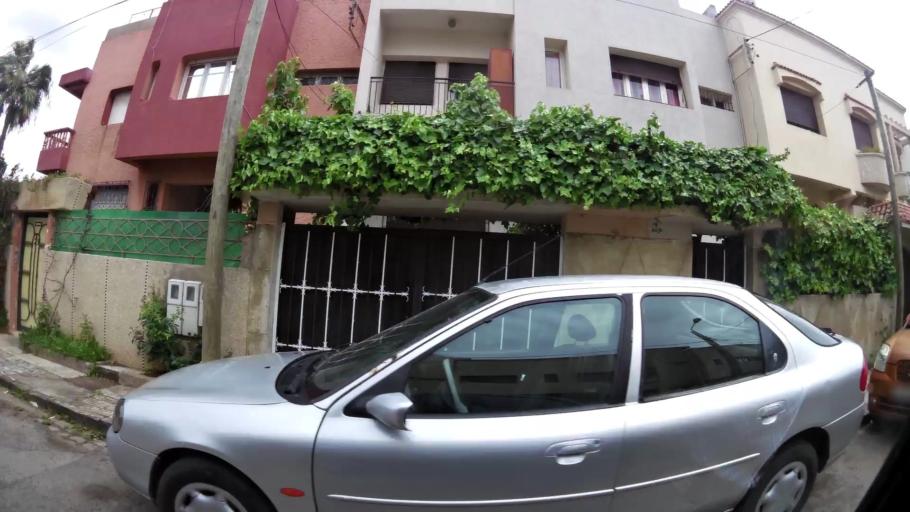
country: MA
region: Grand Casablanca
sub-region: Casablanca
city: Casablanca
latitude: 33.5716
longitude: -7.6668
